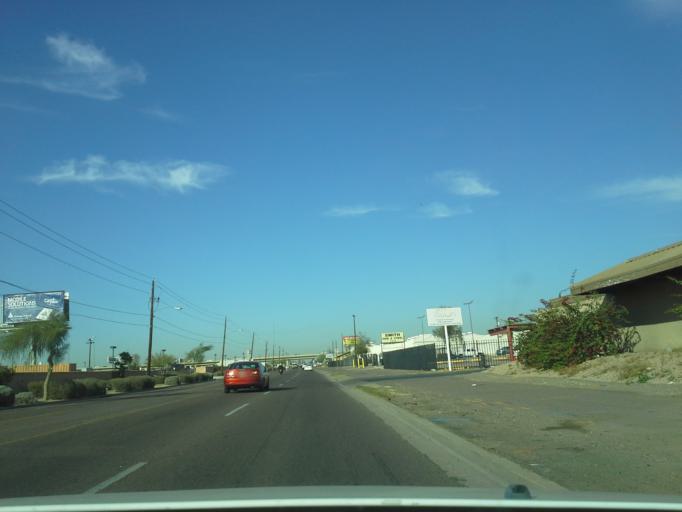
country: US
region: Arizona
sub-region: Maricopa County
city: Phoenix
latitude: 33.4563
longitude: -112.1000
